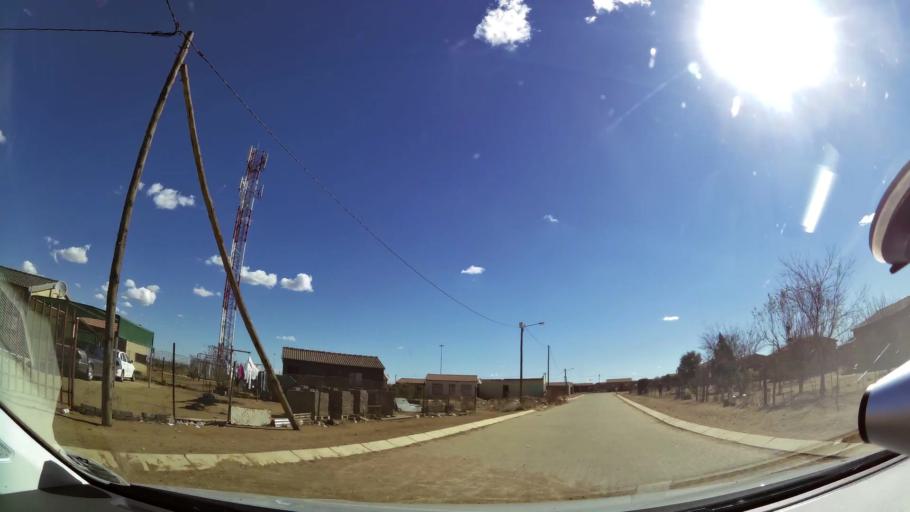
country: ZA
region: North-West
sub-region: Dr Kenneth Kaunda District Municipality
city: Klerksdorp
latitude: -26.8719
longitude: 26.5677
